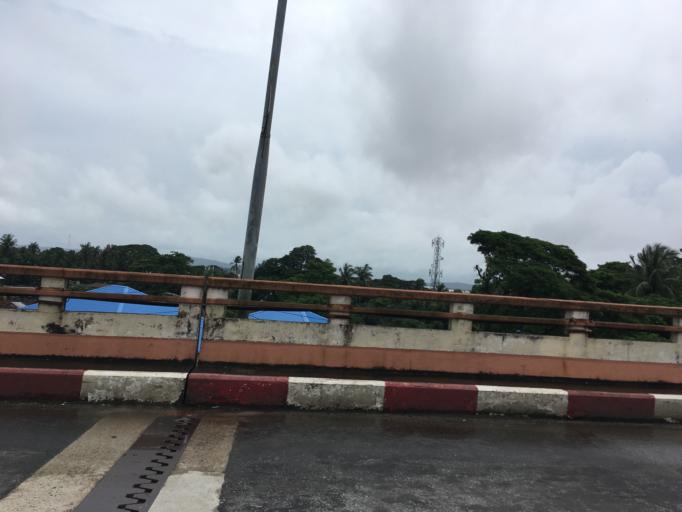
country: MM
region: Mon
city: Mawlamyine
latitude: 16.5002
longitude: 97.6230
